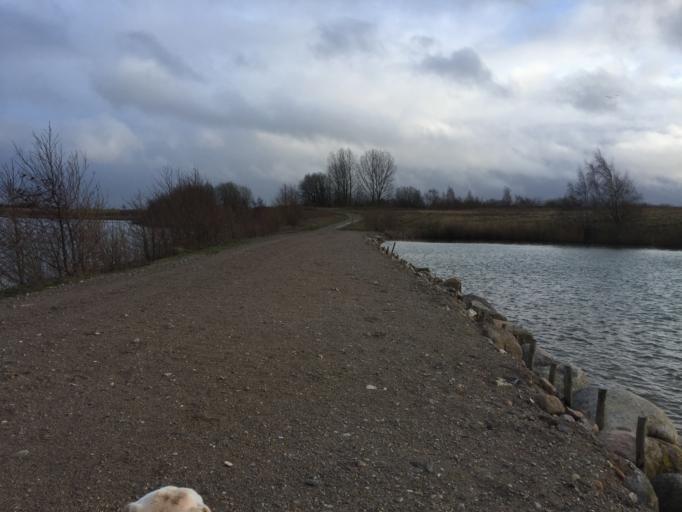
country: DK
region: South Denmark
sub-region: Kerteminde Kommune
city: Langeskov
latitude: 55.3294
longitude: 10.5327
